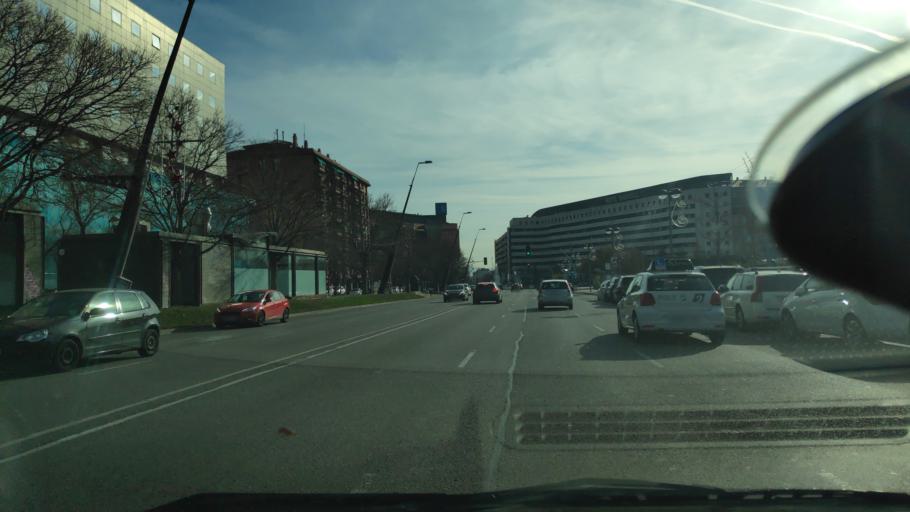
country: ES
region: Catalonia
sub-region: Provincia de Barcelona
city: Sabadell
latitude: 41.5521
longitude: 2.0979
